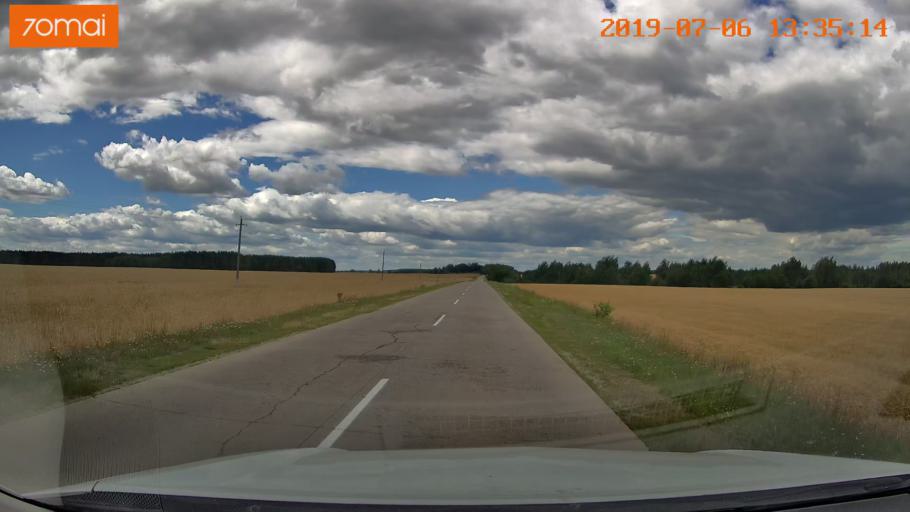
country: BY
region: Minsk
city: Enyerhyetykaw
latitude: 53.6806
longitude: 26.8841
